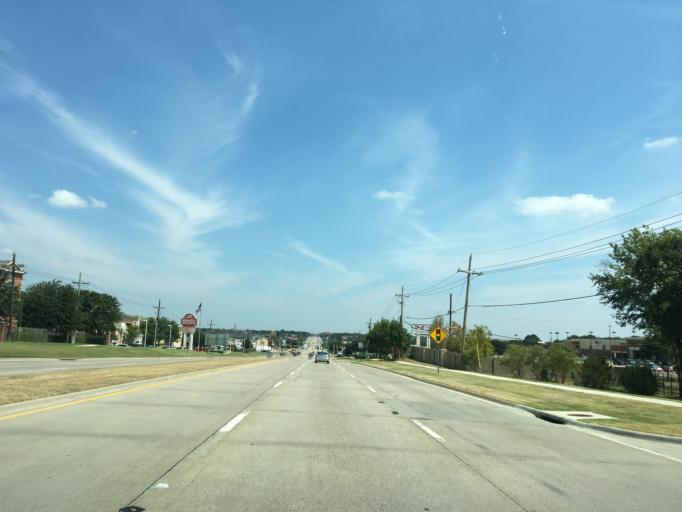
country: US
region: Texas
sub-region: Denton County
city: Lewisville
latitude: 33.0086
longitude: -96.9930
